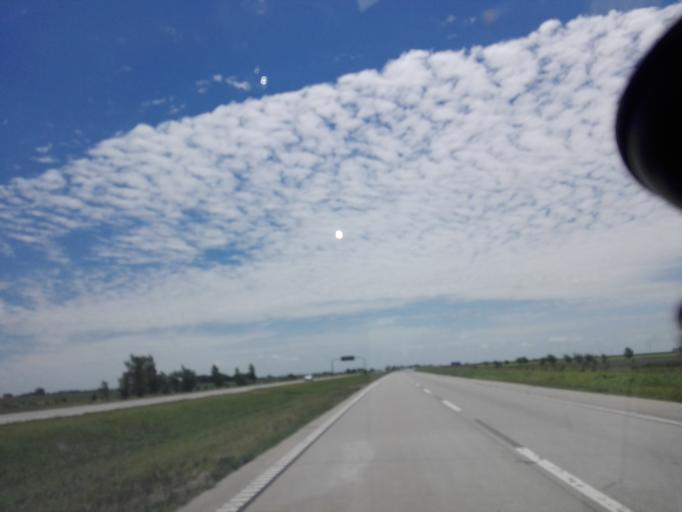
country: AR
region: Cordoba
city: Villa Maria
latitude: -32.3494
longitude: -63.2465
